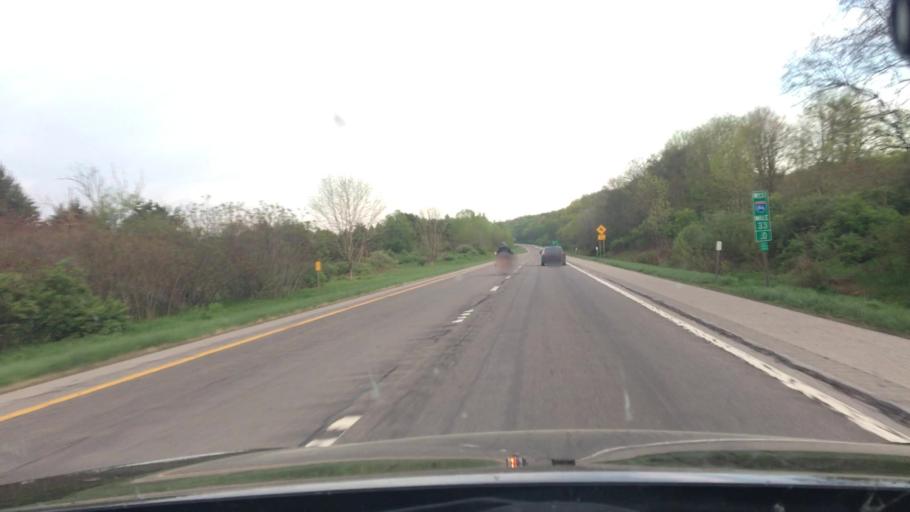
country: US
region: New York
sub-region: Chautauqua County
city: Falconer
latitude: 42.1362
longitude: -79.1507
